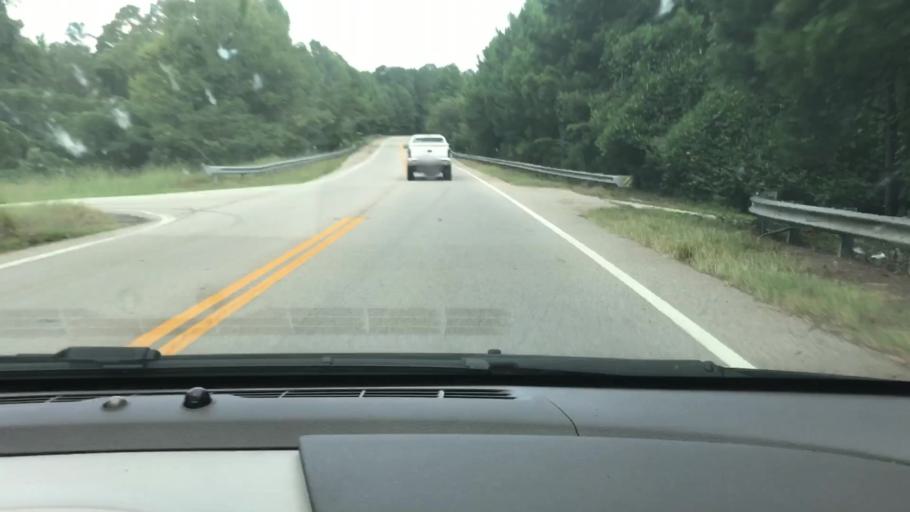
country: US
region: Georgia
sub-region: Troup County
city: La Grange
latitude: 32.9714
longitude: -85.0248
